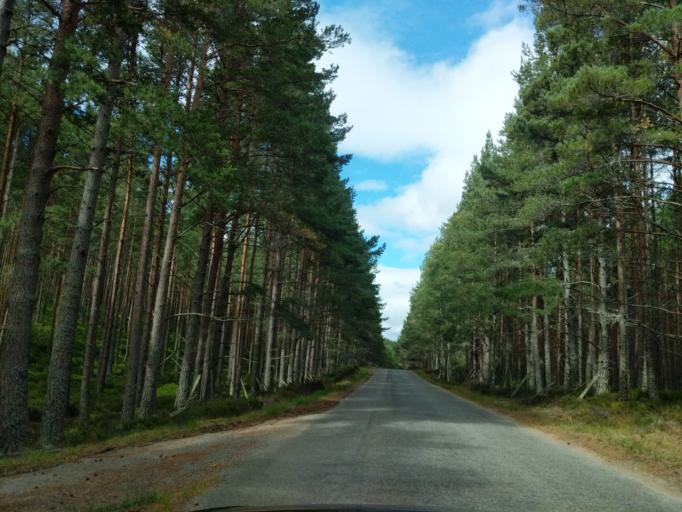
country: GB
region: Scotland
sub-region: Aberdeenshire
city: Ballater
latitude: 57.0485
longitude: -3.1210
